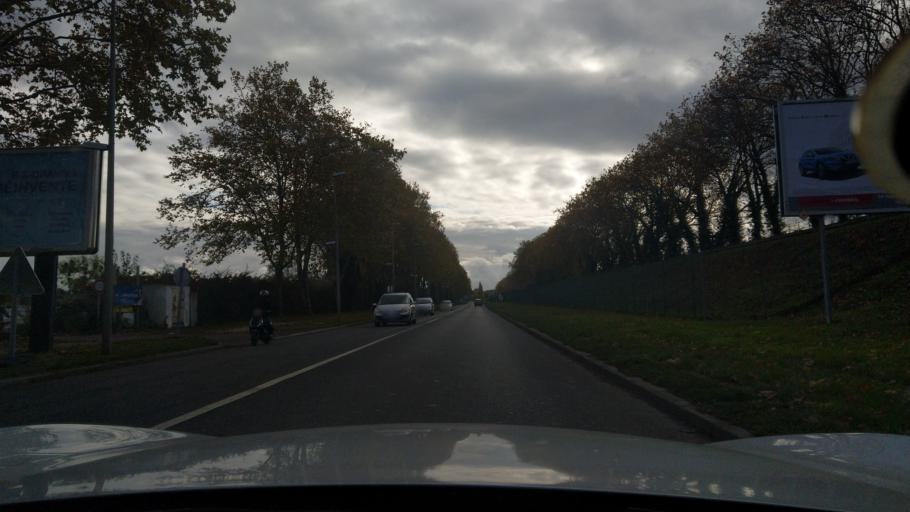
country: FR
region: Ile-de-France
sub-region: Departement de l'Essonne
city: Grigny
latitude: 48.6362
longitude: 2.3945
